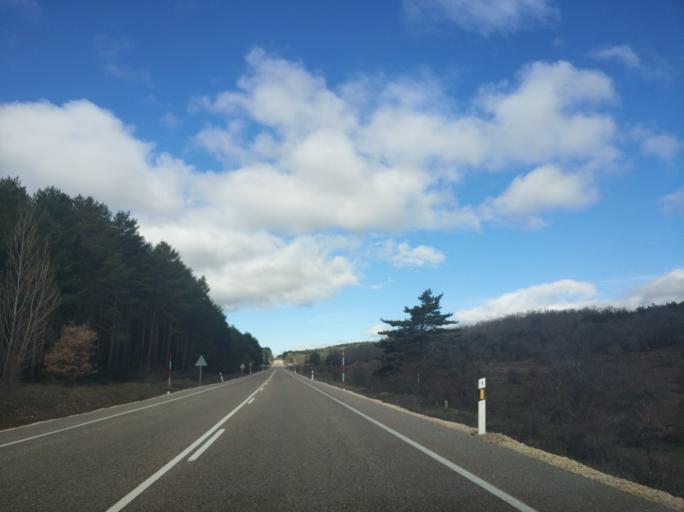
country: ES
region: Castille and Leon
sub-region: Provincia de Burgos
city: Rabanera del Pinar
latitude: 41.8851
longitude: -3.2311
